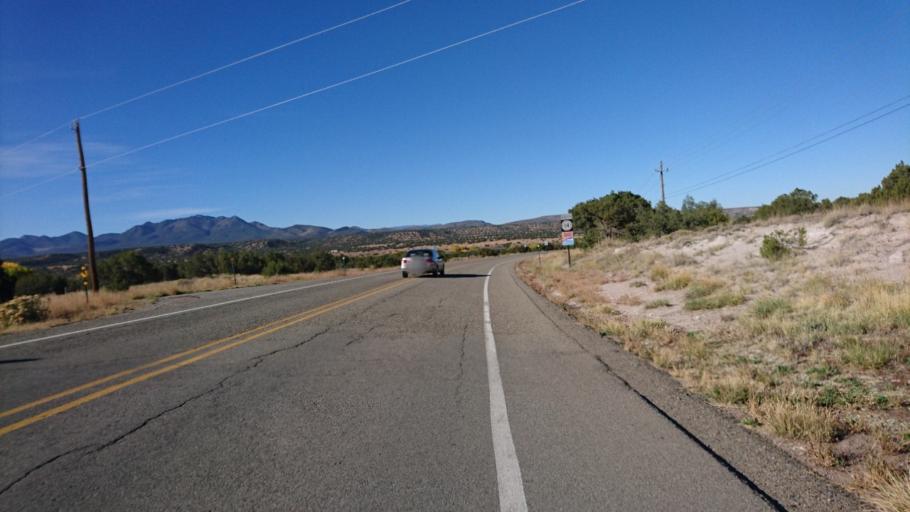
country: US
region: New Mexico
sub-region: Santa Fe County
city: La Cienega
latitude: 35.4303
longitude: -106.0894
